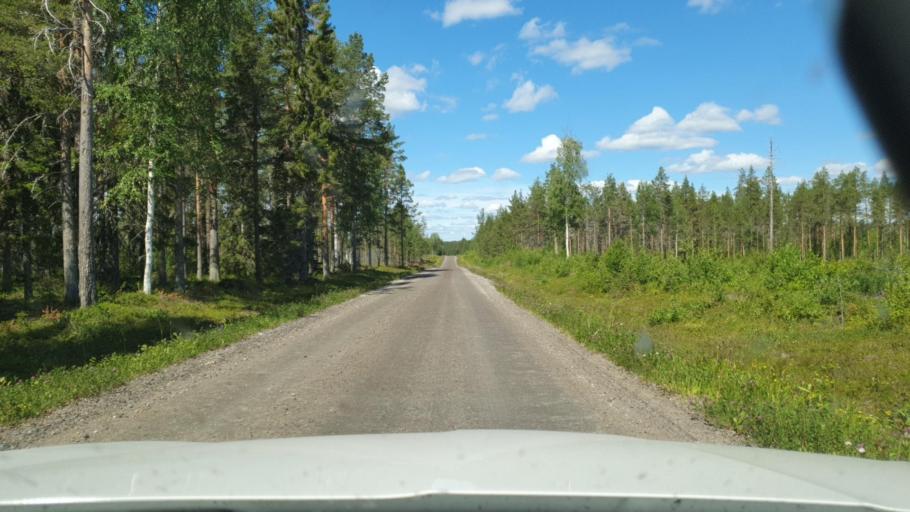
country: SE
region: Vaesterbotten
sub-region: Skelleftea Kommun
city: Byske
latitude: 65.1337
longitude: 21.1929
